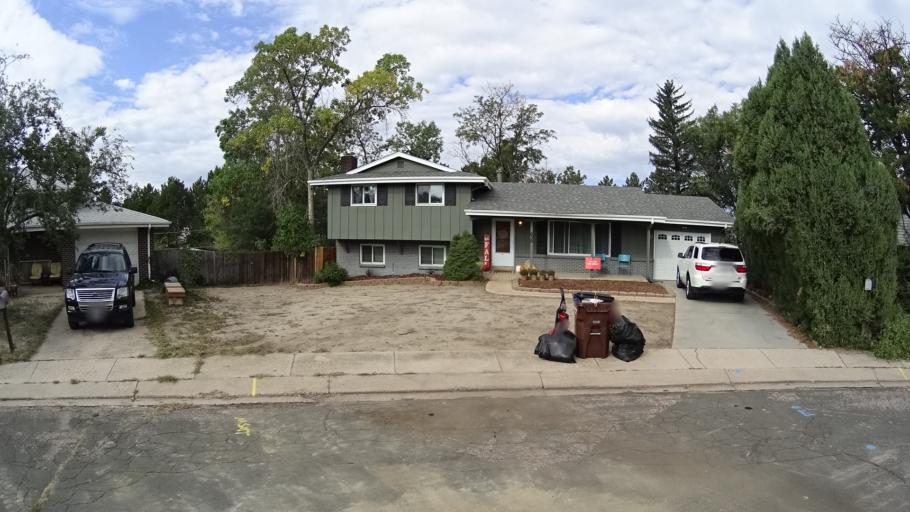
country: US
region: Colorado
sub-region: El Paso County
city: Cimarron Hills
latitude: 38.8437
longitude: -104.7539
